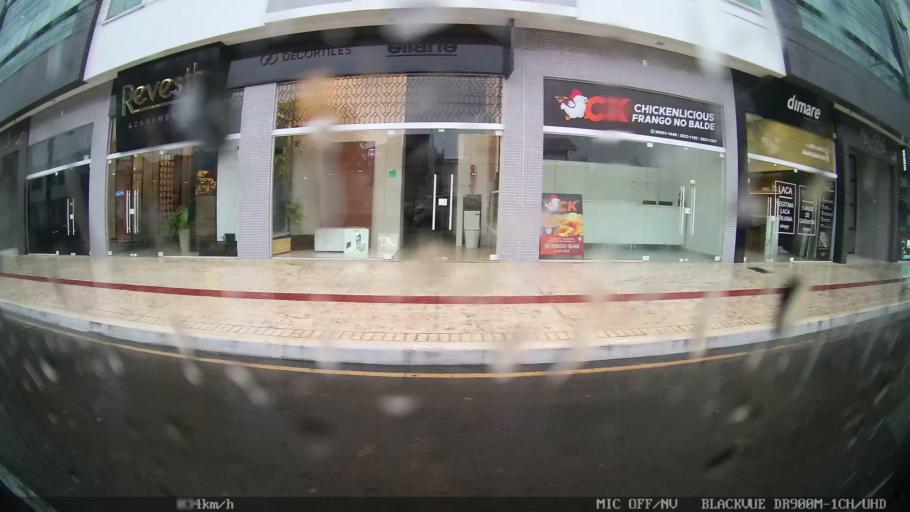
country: BR
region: Santa Catarina
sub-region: Balneario Camboriu
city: Balneario Camboriu
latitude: -26.9929
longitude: -48.6395
